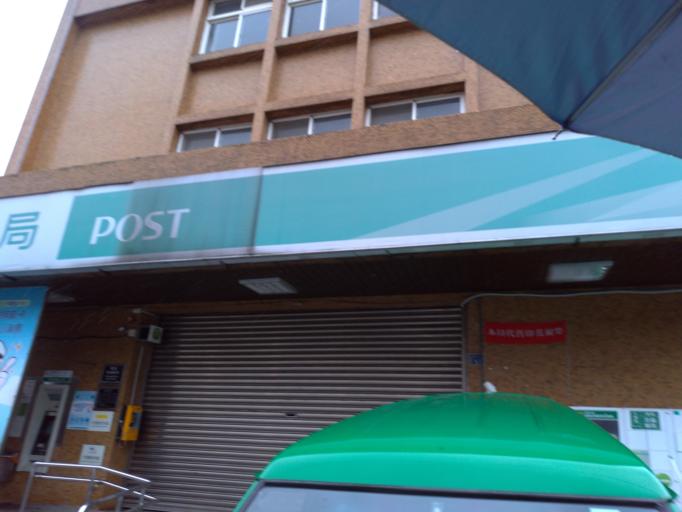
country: TW
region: Taiwan
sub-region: Keelung
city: Keelung
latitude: 25.0842
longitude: 121.6978
